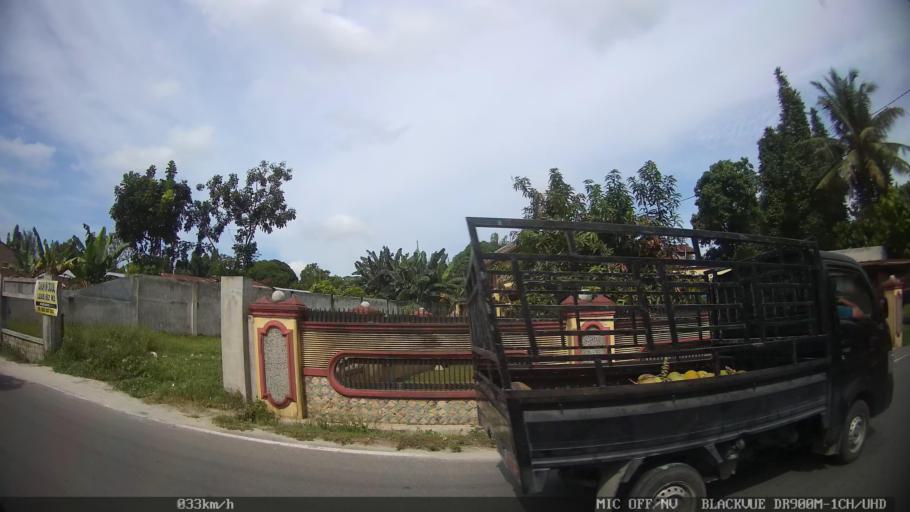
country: ID
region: North Sumatra
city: Percut
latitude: 3.6029
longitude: 98.8574
